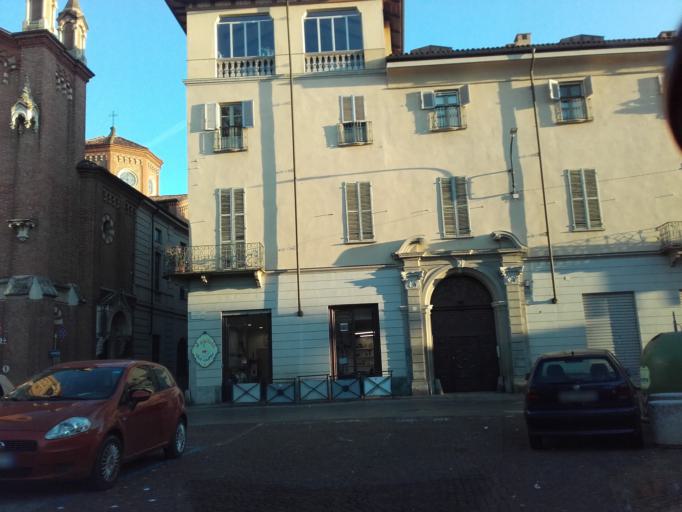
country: IT
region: Piedmont
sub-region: Provincia di Asti
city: Asti
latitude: 44.8991
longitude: 8.1976
